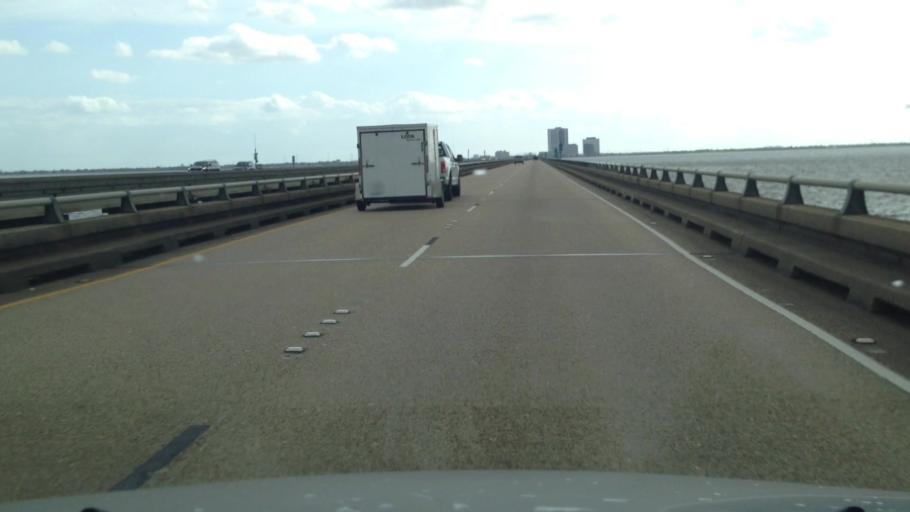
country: US
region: Louisiana
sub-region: Jefferson Parish
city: Metairie
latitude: 30.0534
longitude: -90.1487
